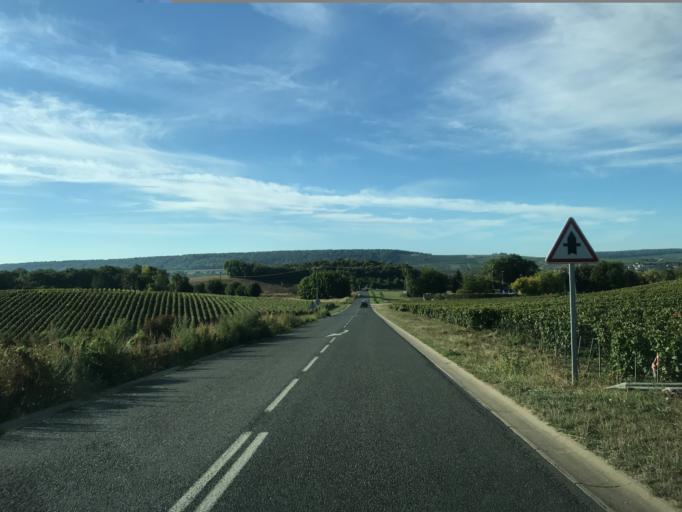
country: FR
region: Champagne-Ardenne
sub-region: Departement de la Marne
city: Chatillon-sur-Marne
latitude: 49.0996
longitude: 3.7672
